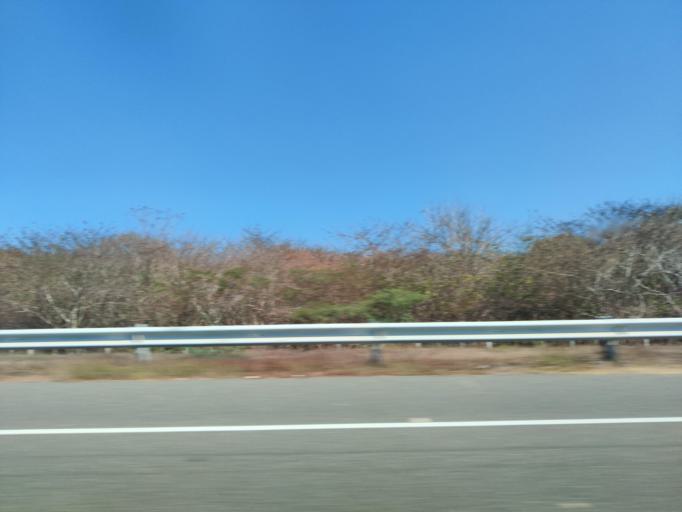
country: CO
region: Atlantico
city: Puerto Colombia
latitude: 10.9684
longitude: -74.9921
